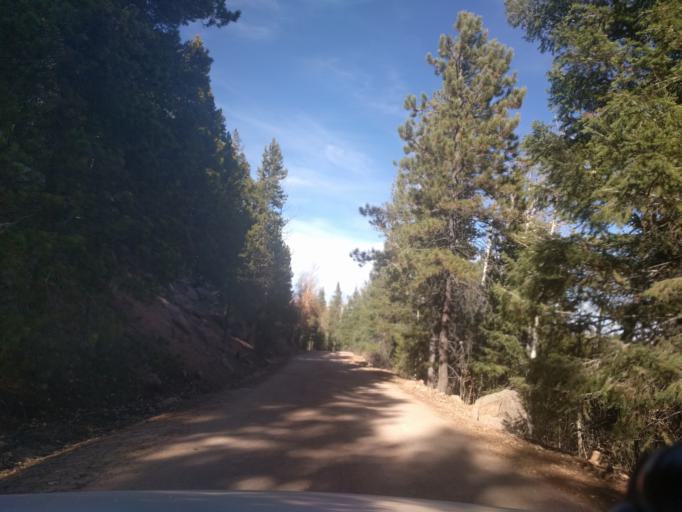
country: US
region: Colorado
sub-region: Douglas County
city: Perry Park
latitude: 39.2009
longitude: -105.0511
